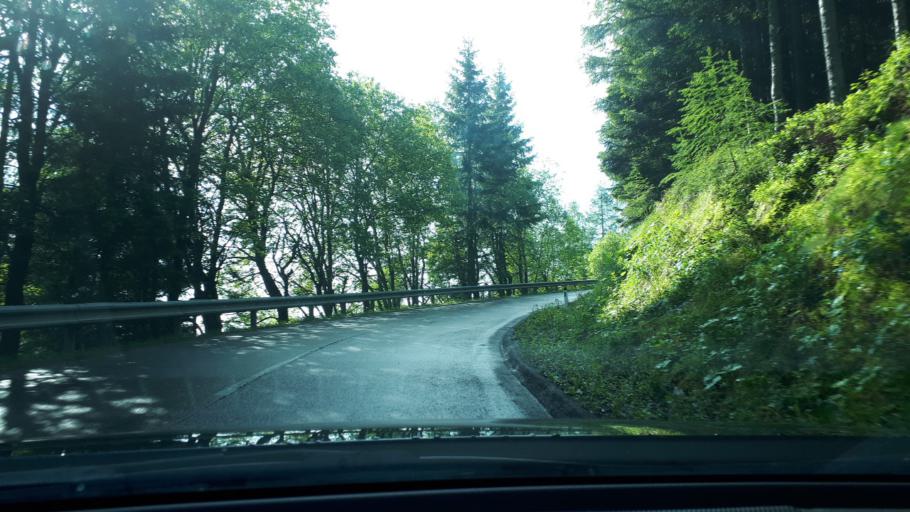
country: AT
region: Styria
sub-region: Politischer Bezirk Voitsberg
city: Modriach
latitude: 46.9257
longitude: 15.0157
